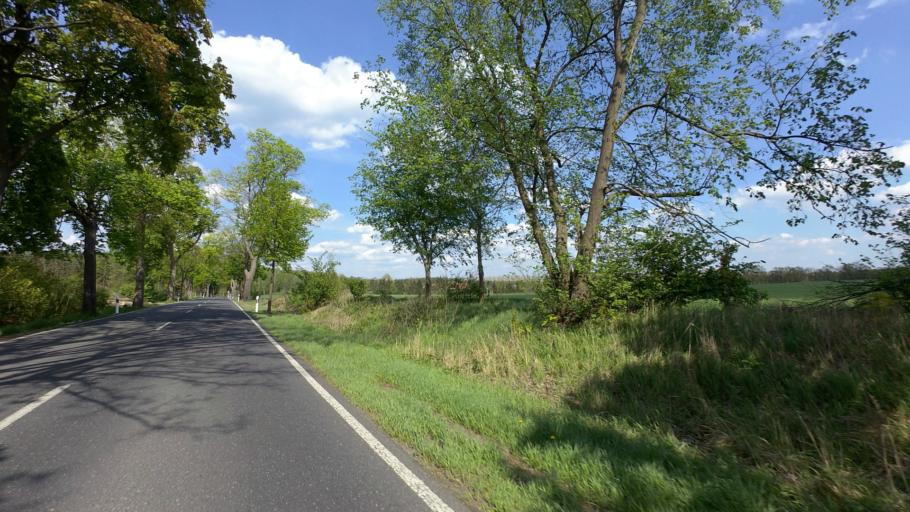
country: DE
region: Brandenburg
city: Marienwerder
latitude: 52.8833
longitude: 13.5447
